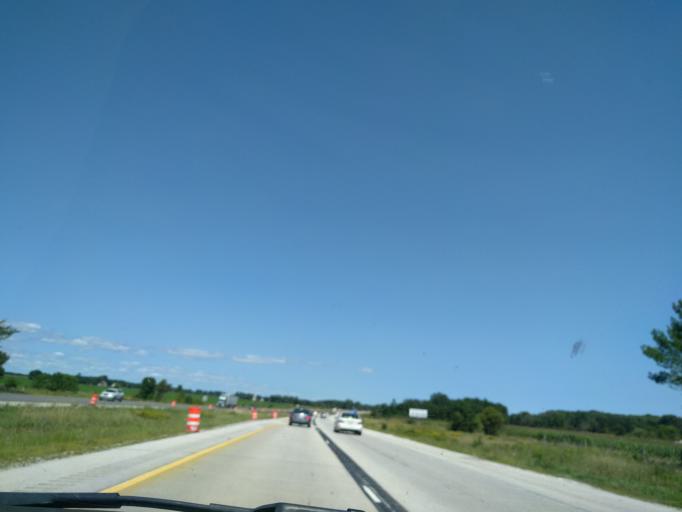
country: US
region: Wisconsin
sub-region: Manitowoc County
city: Cleveland
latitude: 43.9972
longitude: -87.7279
